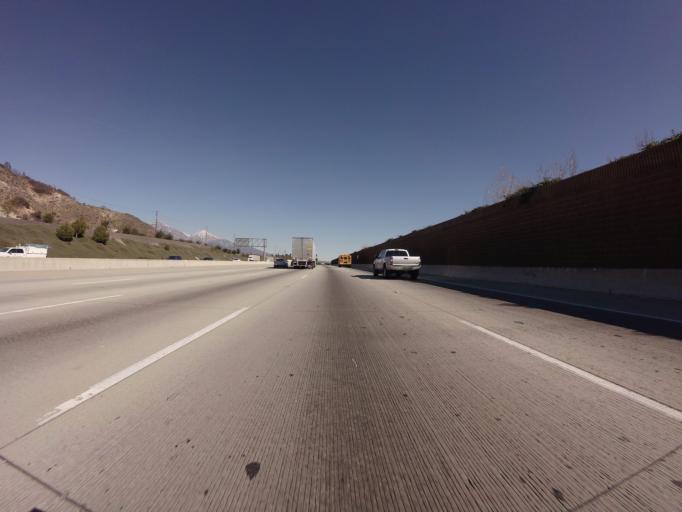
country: US
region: California
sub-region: San Bernardino County
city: San Antonio Heights
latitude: 34.1343
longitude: -117.6751
